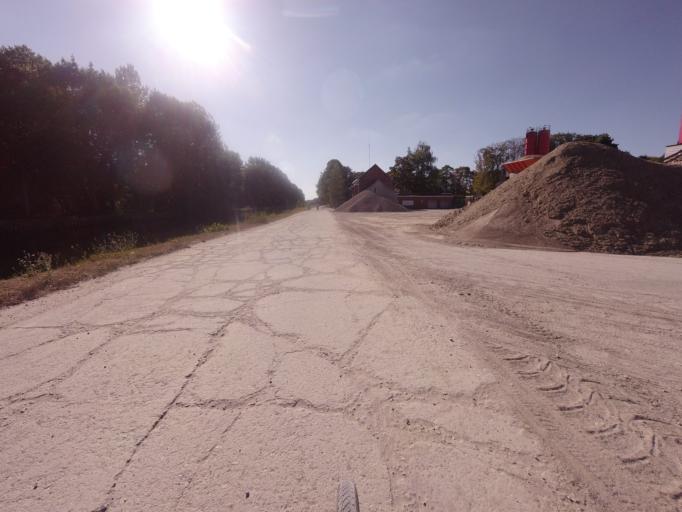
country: BE
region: Flanders
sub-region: Provincie Antwerpen
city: Vosselaar
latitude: 51.3298
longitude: 4.8924
